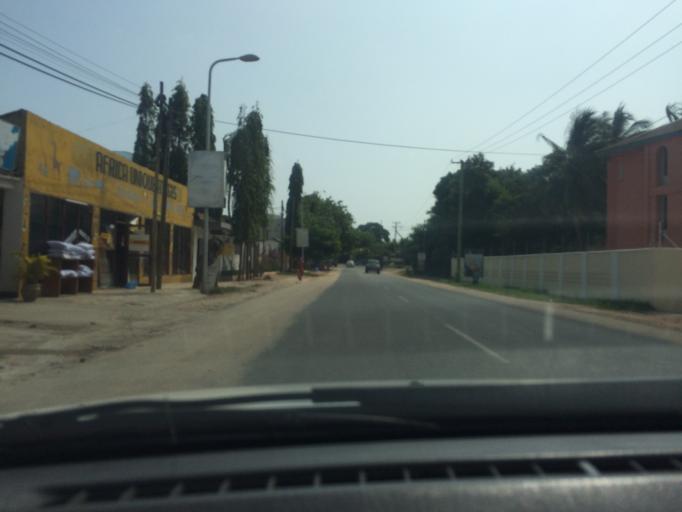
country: TZ
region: Dar es Salaam
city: Magomeni
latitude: -6.7543
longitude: 39.2744
